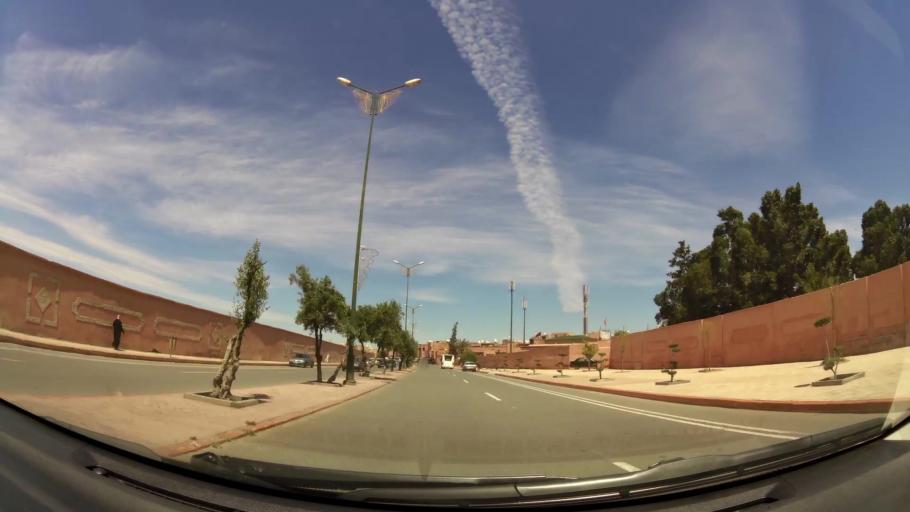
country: MA
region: Marrakech-Tensift-Al Haouz
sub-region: Marrakech
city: Marrakesh
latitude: 31.6178
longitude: -7.9728
